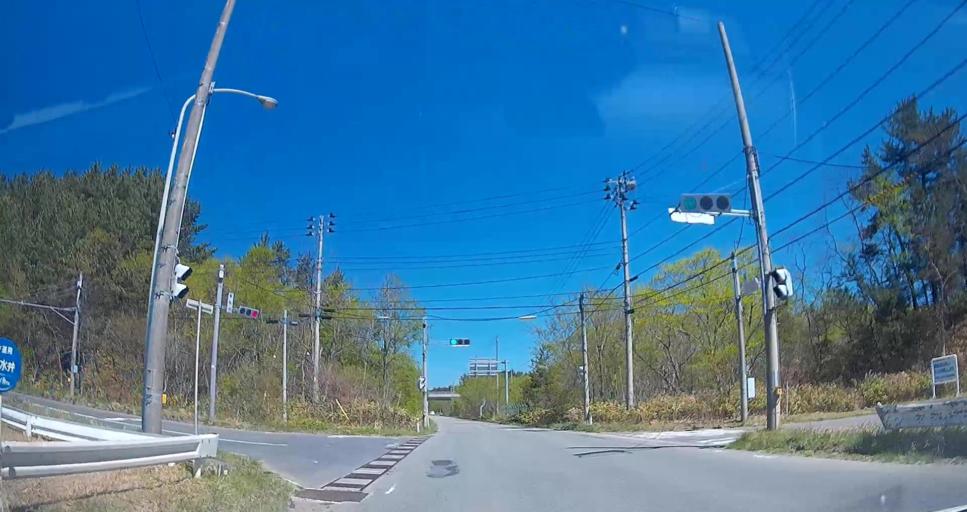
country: JP
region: Aomori
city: Misawa
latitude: 40.9438
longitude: 141.3757
